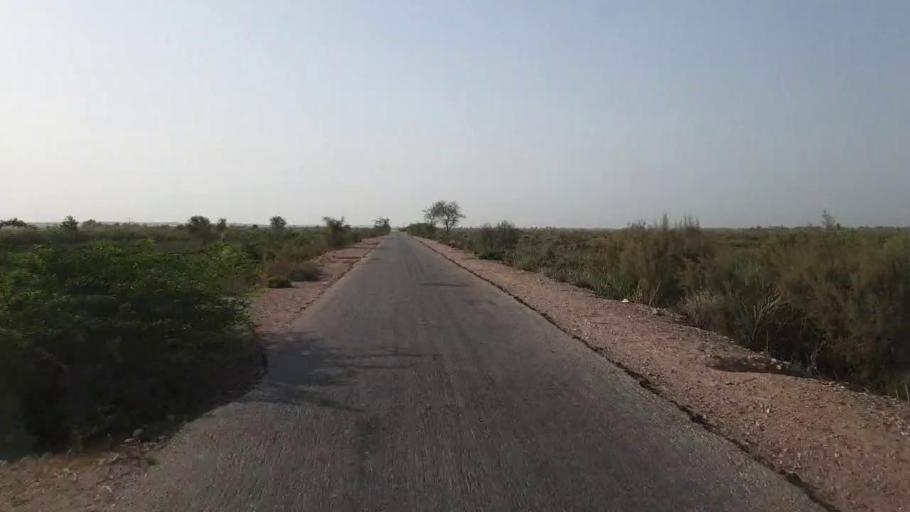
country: PK
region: Sindh
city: Jam Sahib
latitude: 26.4466
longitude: 68.8642
